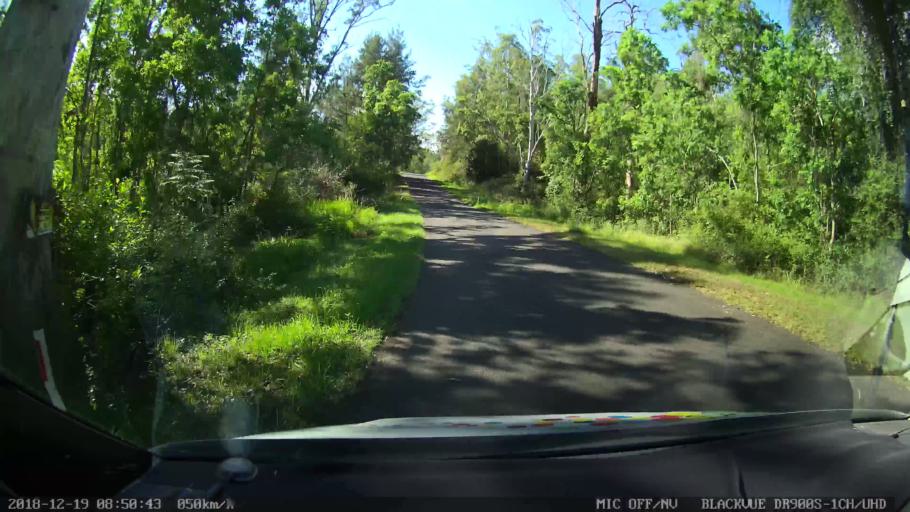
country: AU
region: New South Wales
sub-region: Kyogle
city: Kyogle
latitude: -28.3829
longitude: 152.9761
